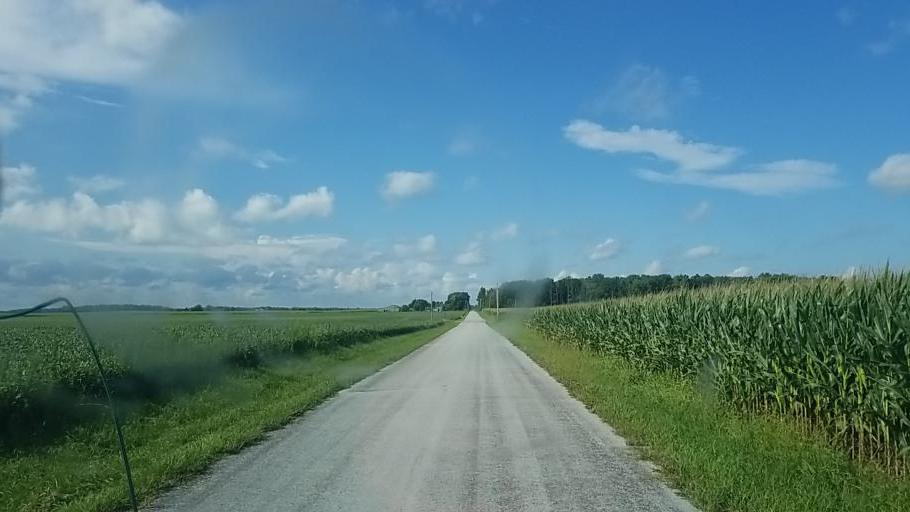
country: US
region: Ohio
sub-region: Hardin County
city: Kenton
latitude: 40.6862
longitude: -83.5309
